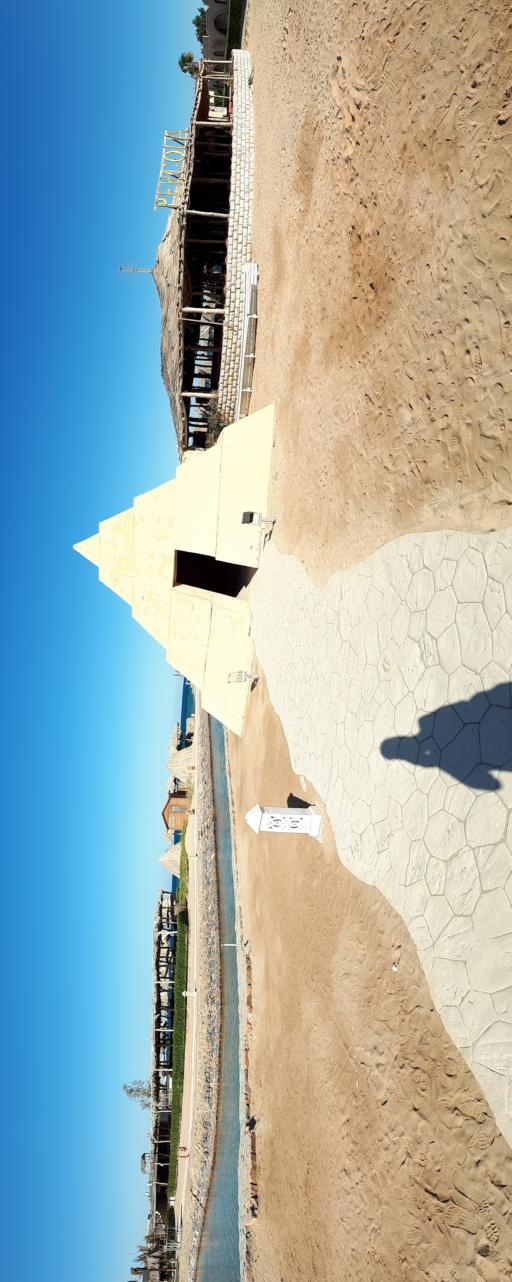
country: EG
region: Red Sea
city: Makadi Bay
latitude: 27.1078
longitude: 33.8310
